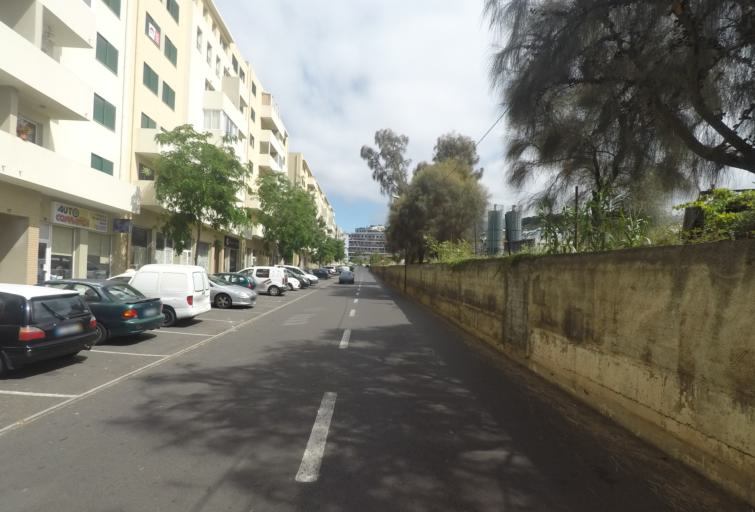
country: PT
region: Madeira
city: Camara de Lobos
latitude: 32.6457
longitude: -16.9397
